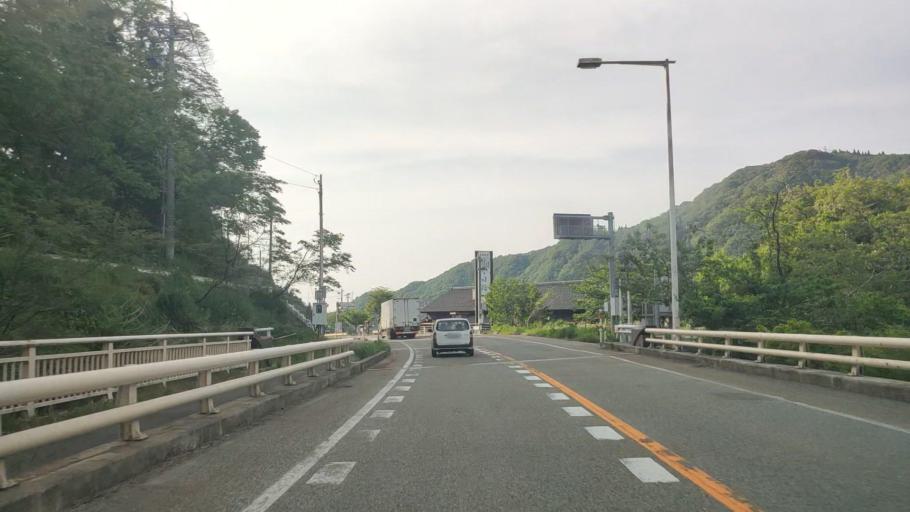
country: JP
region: Toyama
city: Yatsuomachi-higashikumisaka
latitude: 36.5459
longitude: 137.2275
